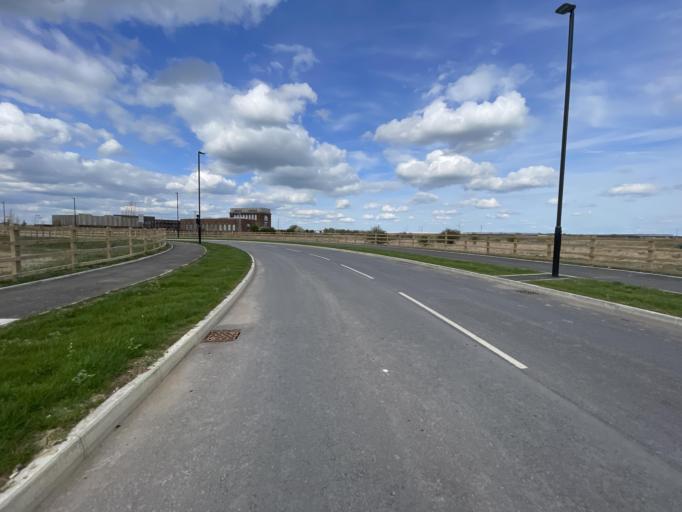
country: GB
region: England
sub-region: Warwickshire
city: Rugby
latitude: 52.3648
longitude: -1.1900
